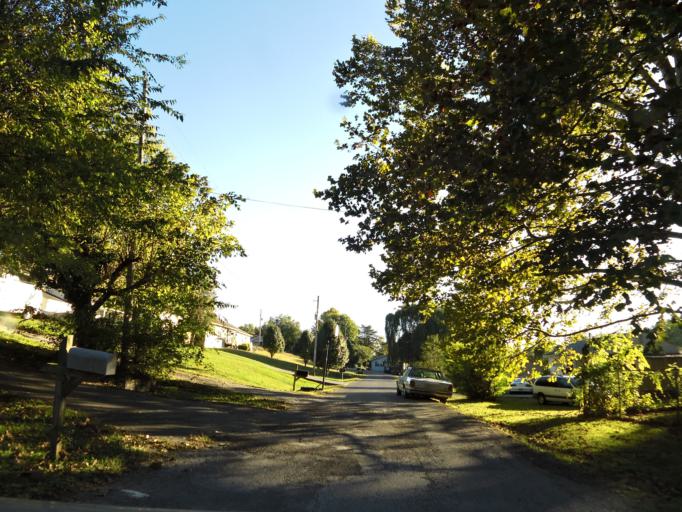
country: US
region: Tennessee
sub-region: Blount County
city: Eagleton Village
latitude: 35.7885
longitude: -83.9520
